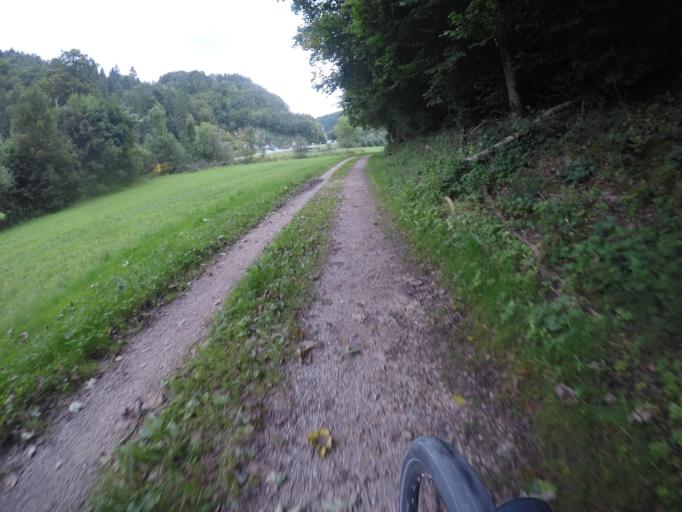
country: DE
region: Baden-Wuerttemberg
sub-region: Tuebingen Region
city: Munsingen
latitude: 48.4479
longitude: 9.4491
